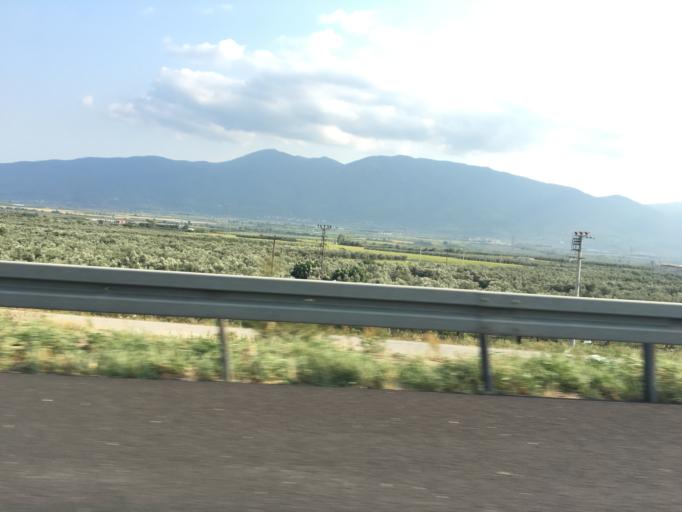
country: TR
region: Bursa
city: Orhangazi
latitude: 40.4594
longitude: 29.2937
